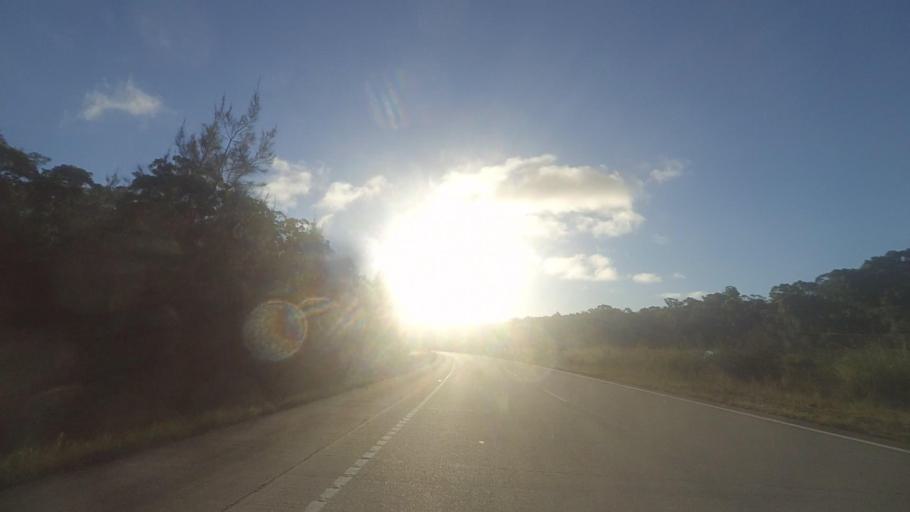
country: AU
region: New South Wales
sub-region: Great Lakes
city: Hawks Nest
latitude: -32.5480
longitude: 152.1567
